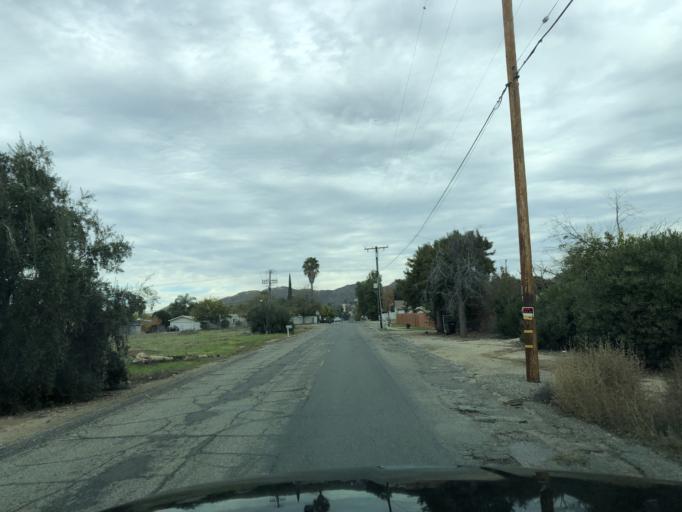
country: US
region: California
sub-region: Riverside County
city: Wildomar
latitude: 33.6184
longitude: -117.2711
